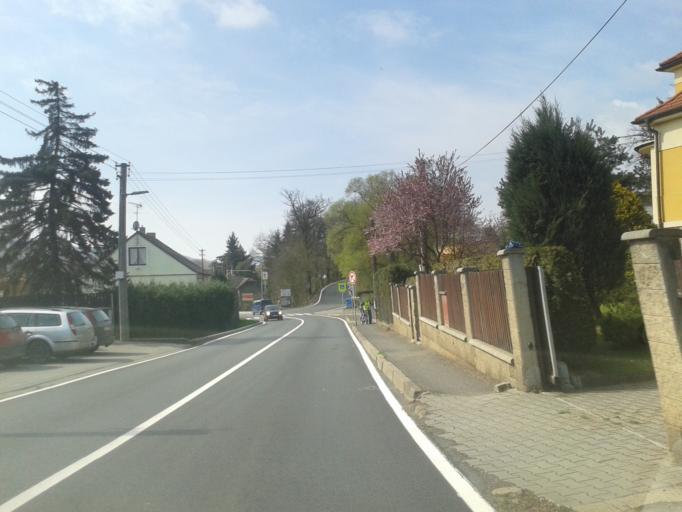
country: CZ
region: Central Bohemia
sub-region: Okres Beroun
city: Horovice
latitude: 49.8453
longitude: 13.9056
